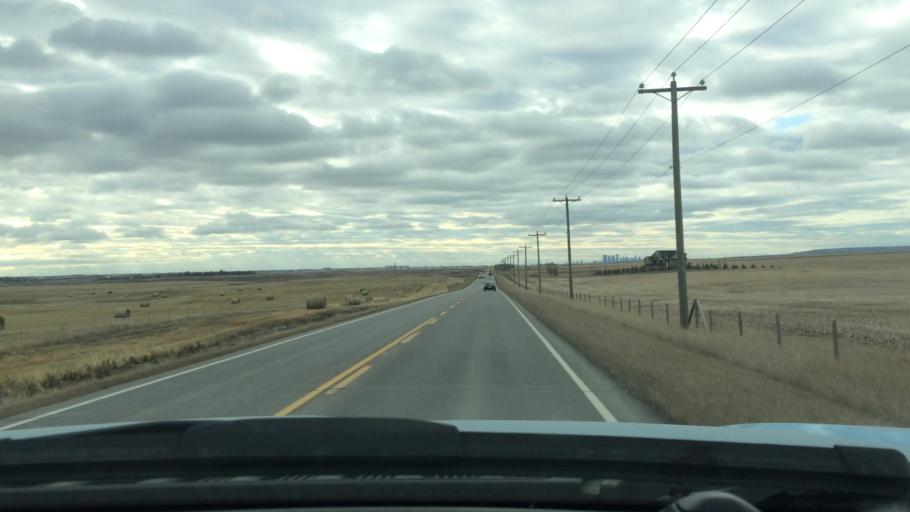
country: CA
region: Alberta
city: Airdrie
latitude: 51.2238
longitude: -114.0249
